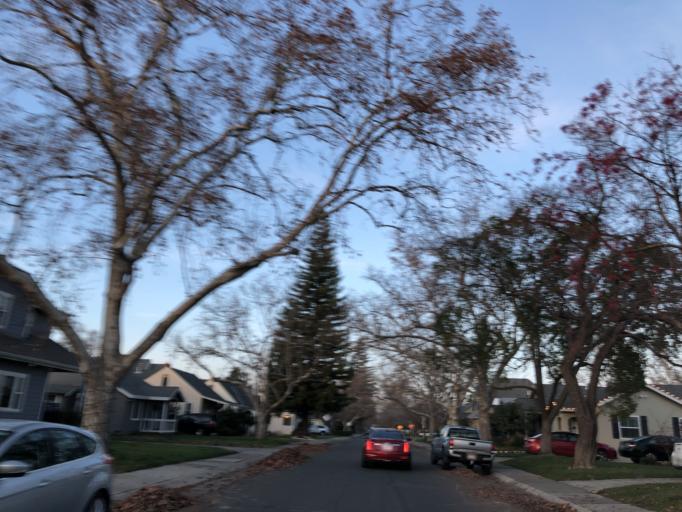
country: US
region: California
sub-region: Sacramento County
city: Sacramento
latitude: 38.5599
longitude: -121.4361
